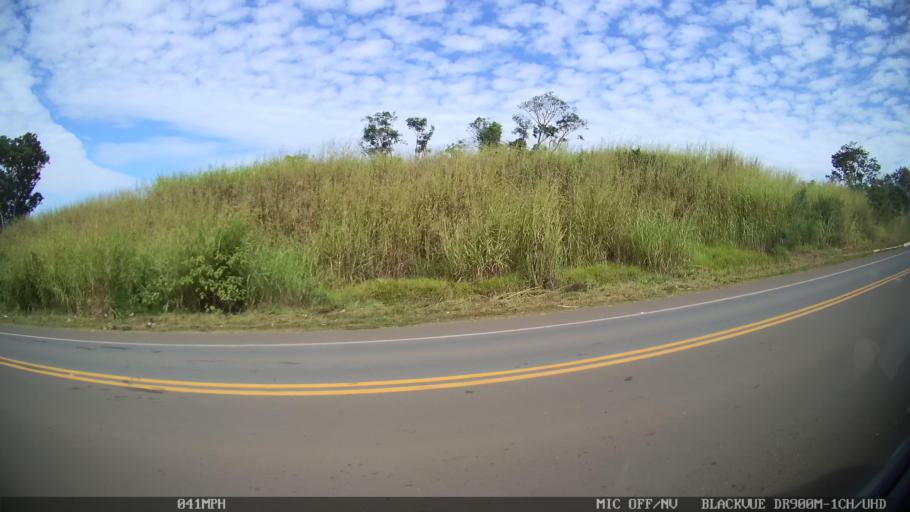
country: BR
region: Sao Paulo
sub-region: Santa Barbara D'Oeste
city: Santa Barbara d'Oeste
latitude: -22.7053
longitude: -47.4439
